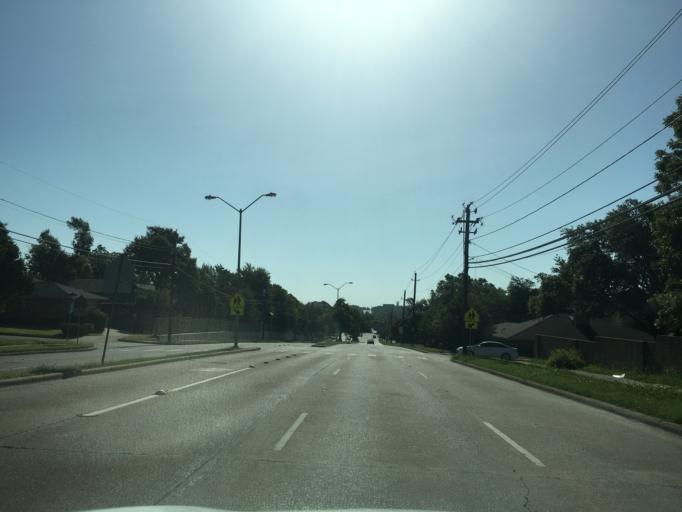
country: US
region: Texas
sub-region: Dallas County
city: Richardson
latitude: 32.8788
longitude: -96.7270
